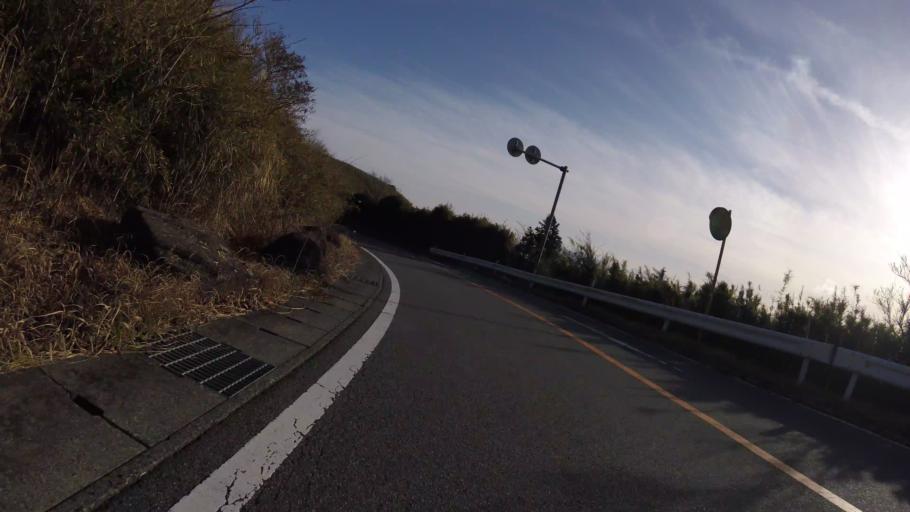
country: JP
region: Kanagawa
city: Yugawara
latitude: 35.1391
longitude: 139.0334
